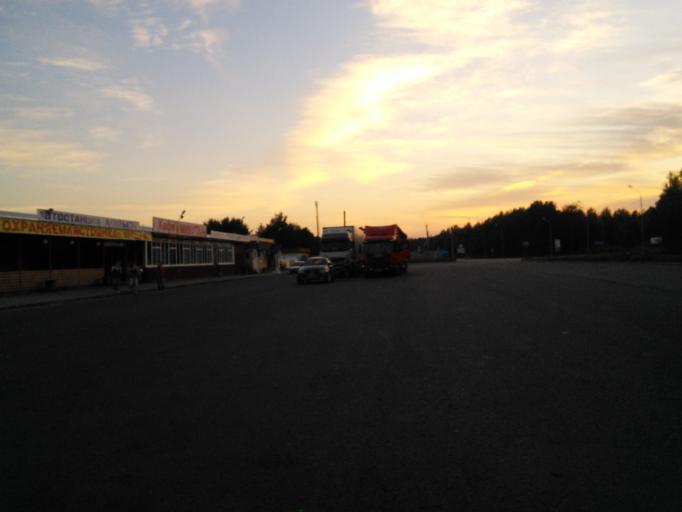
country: RU
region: Vologda
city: Imeni Zhelyabova
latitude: 58.9732
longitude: 36.6012
